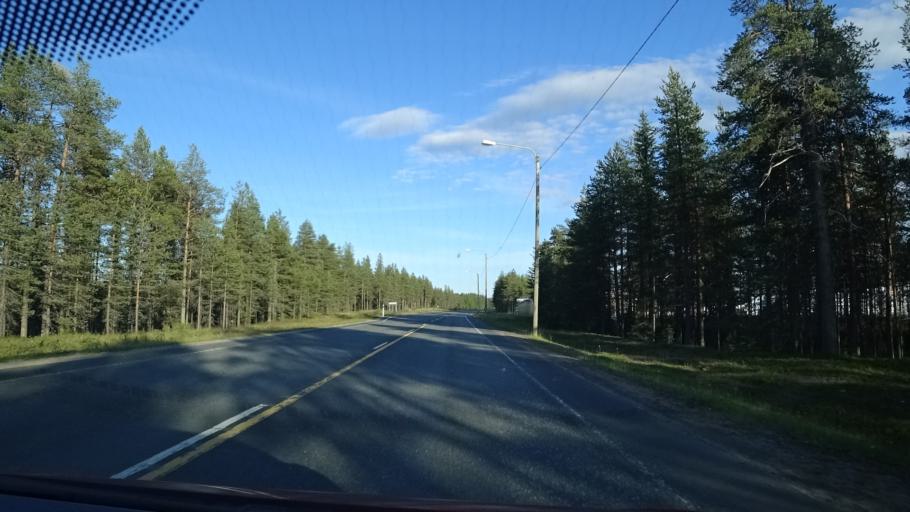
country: FI
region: Northern Ostrobothnia
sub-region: Koillismaa
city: Kuusamo
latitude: 66.0161
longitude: 29.1405
